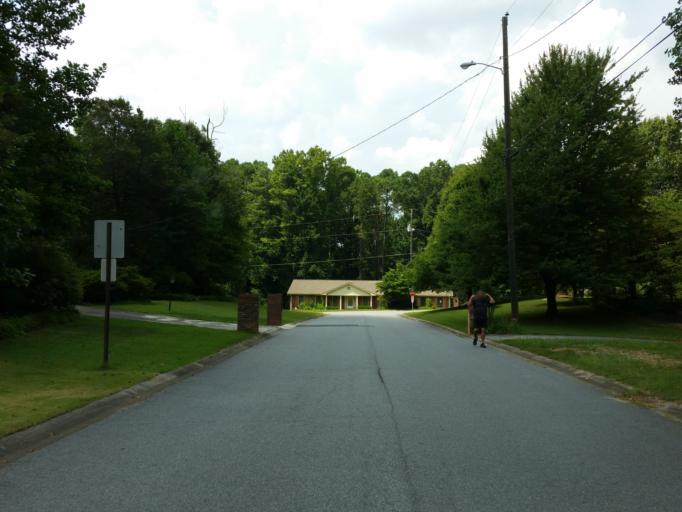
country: US
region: Georgia
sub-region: Cobb County
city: Marietta
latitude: 33.9631
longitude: -84.4742
